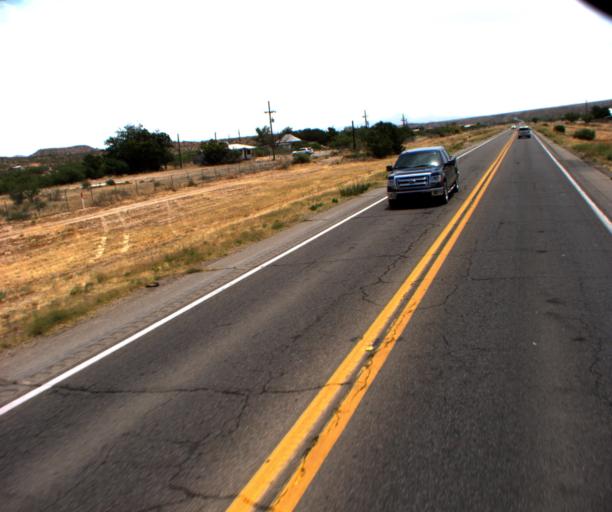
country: US
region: Arizona
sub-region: Gila County
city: Globe
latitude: 33.3550
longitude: -110.6656
